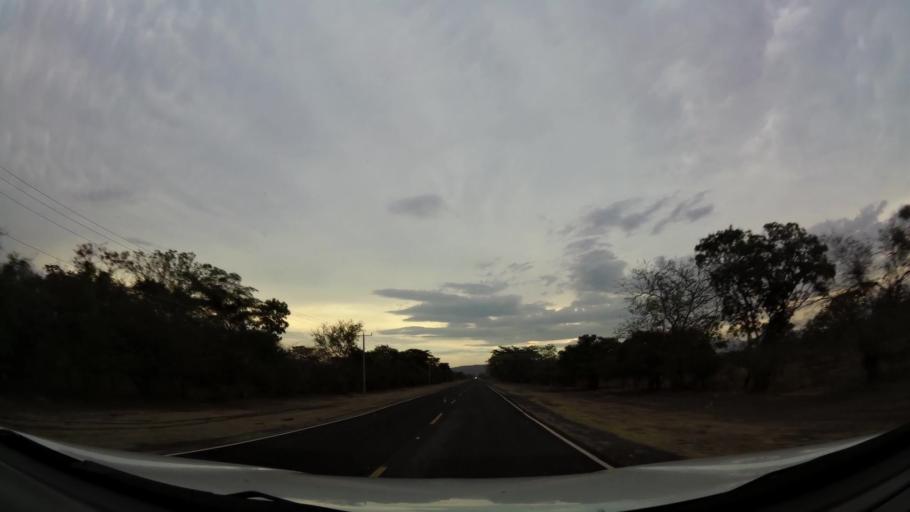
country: NI
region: Matagalpa
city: Ciudad Dario
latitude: 12.8758
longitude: -86.1915
